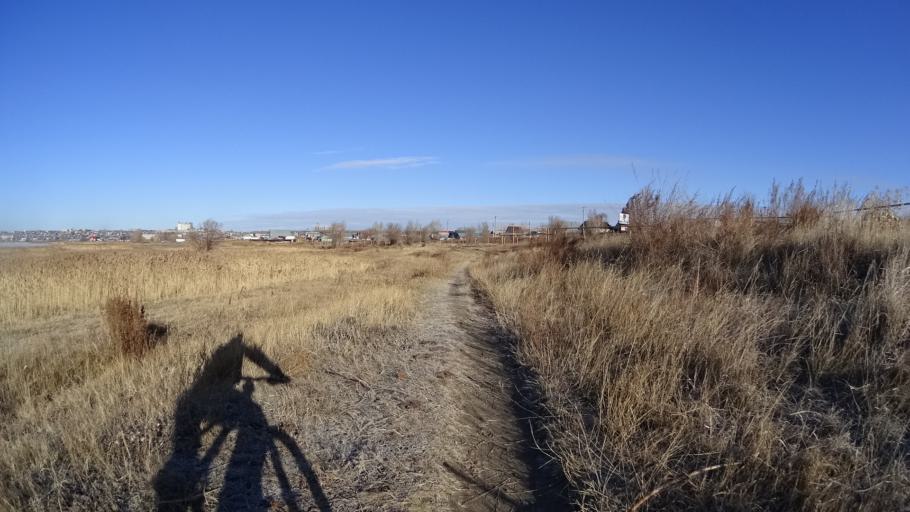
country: RU
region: Chelyabinsk
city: Troitsk
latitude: 54.0836
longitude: 61.5930
